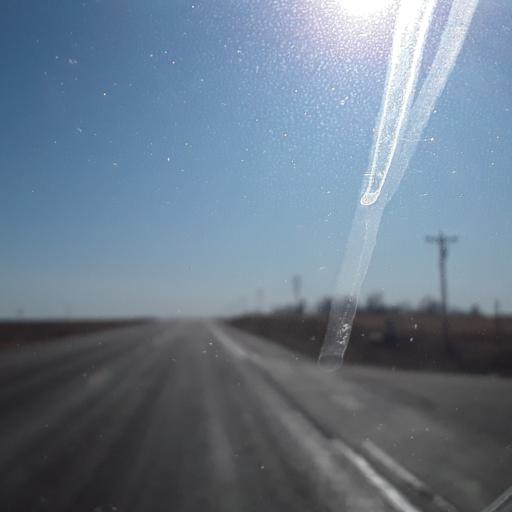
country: US
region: Nebraska
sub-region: Frontier County
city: Stockville
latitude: 40.5338
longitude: -100.6487
